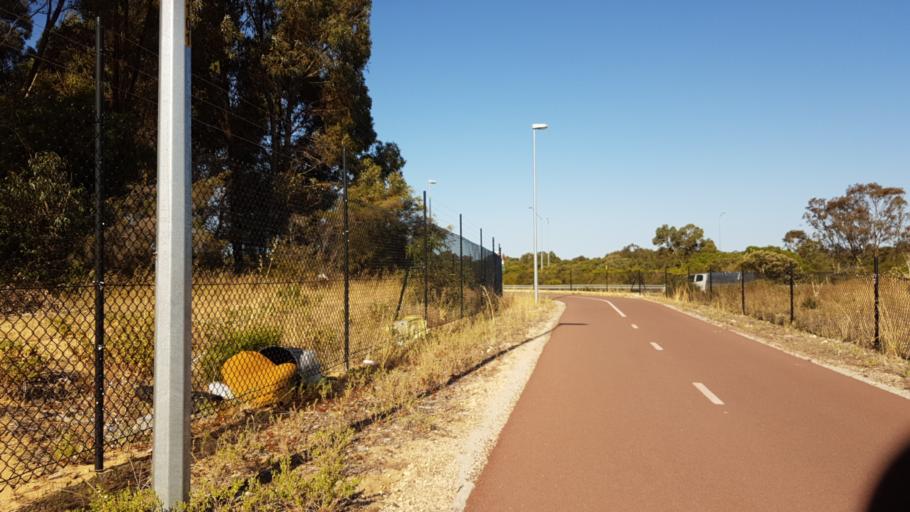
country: AU
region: Western Australia
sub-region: Kwinana
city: Wellard
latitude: -32.3082
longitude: 115.8308
